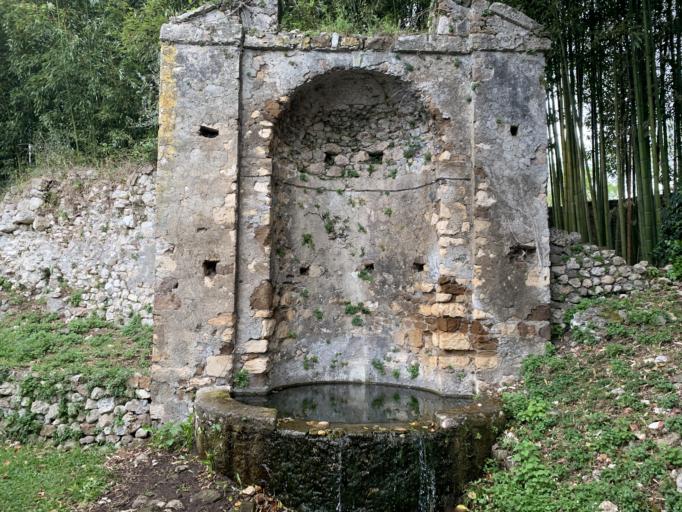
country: IT
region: Latium
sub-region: Provincia di Latina
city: Norma
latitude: 41.5827
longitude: 12.9540
